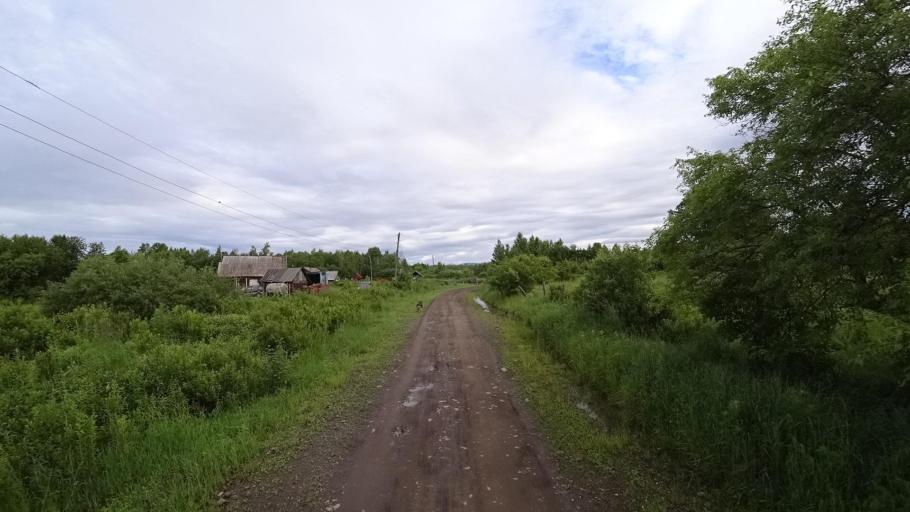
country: RU
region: Khabarovsk Krai
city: Amursk
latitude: 49.8852
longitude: 136.1282
